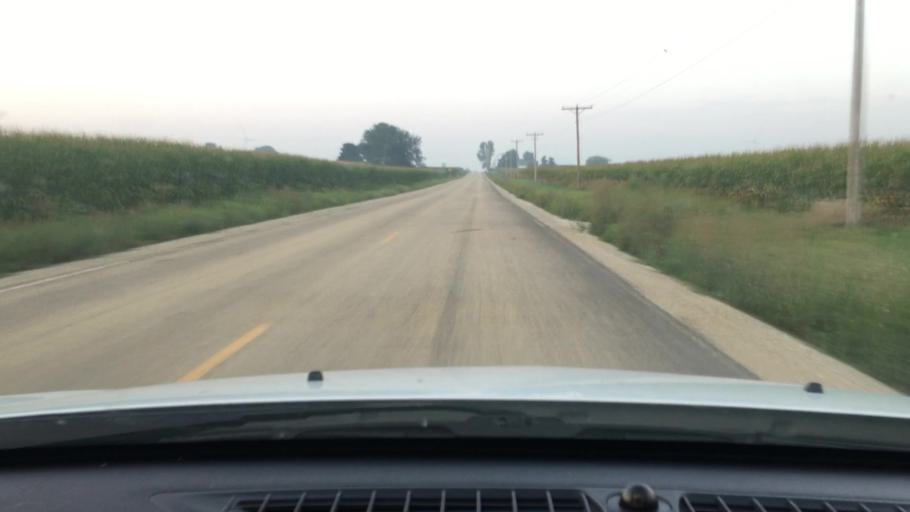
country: US
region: Illinois
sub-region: DeKalb County
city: Waterman
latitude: 41.8410
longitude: -88.7733
